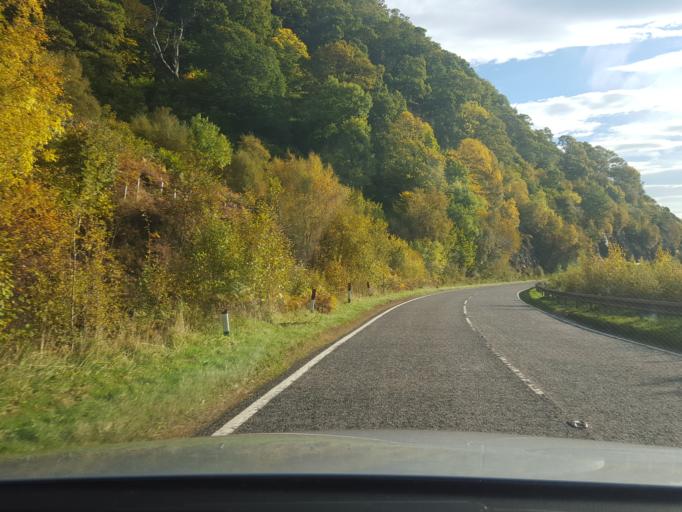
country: GB
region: Scotland
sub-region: Highland
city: Fort William
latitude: 57.2614
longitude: -5.4945
